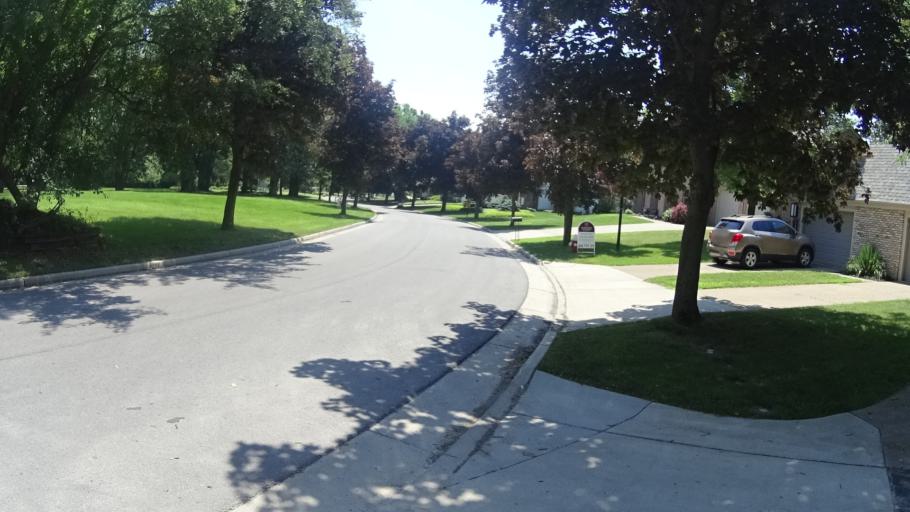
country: US
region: Ohio
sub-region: Erie County
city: Sandusky
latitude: 41.4125
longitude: -82.6382
